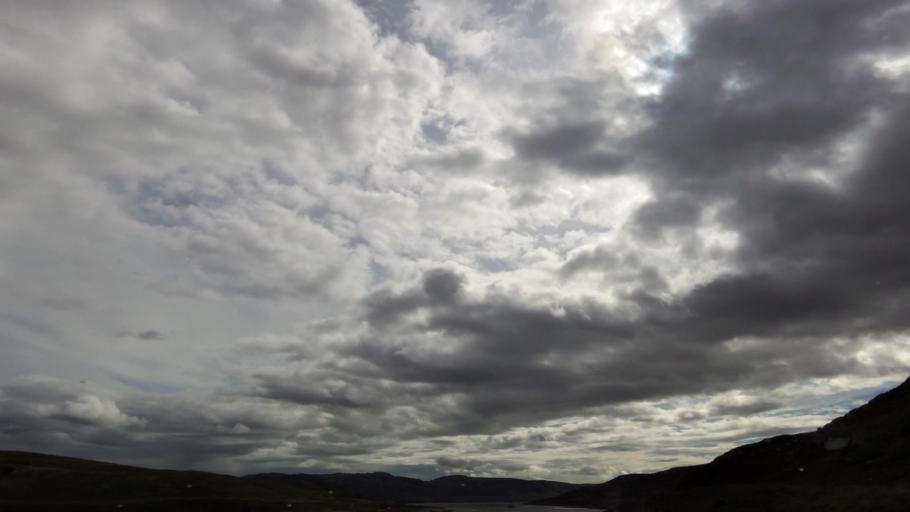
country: IS
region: West
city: Stykkisholmur
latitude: 65.5958
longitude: -22.1241
